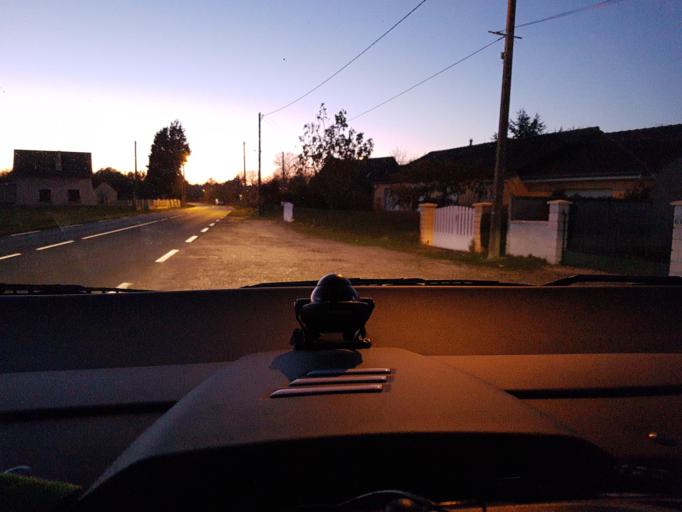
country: FR
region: Picardie
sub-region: Departement de la Somme
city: Cayeux-sur-Mer
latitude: 50.1983
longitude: 1.5325
